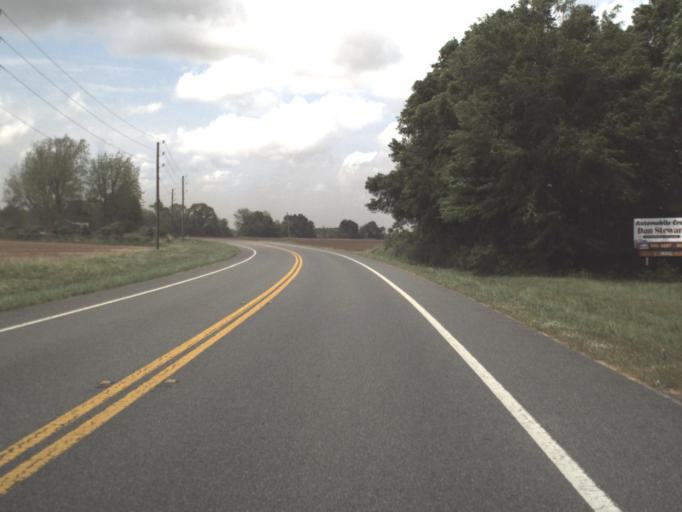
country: US
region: Florida
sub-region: Santa Rosa County
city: Point Baker
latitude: 30.8017
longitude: -87.0928
